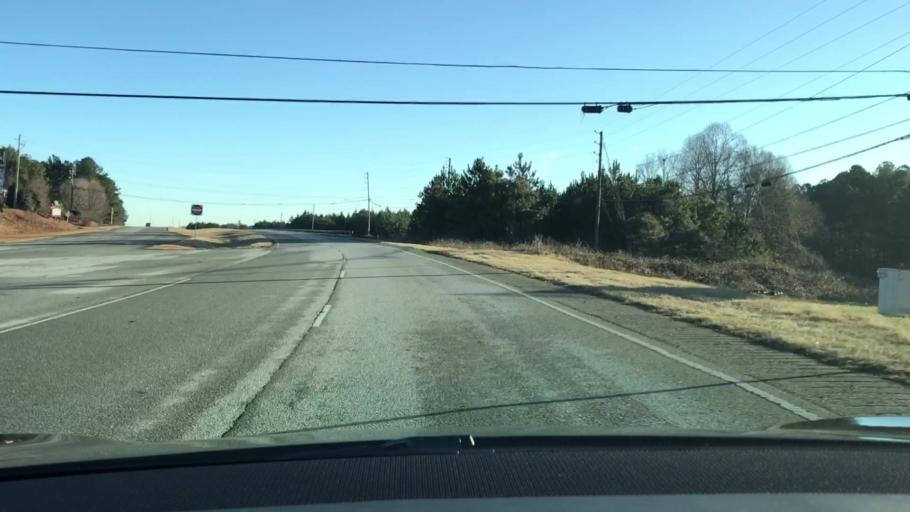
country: US
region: Georgia
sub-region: Gwinnett County
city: Buford
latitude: 34.1448
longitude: -83.9777
